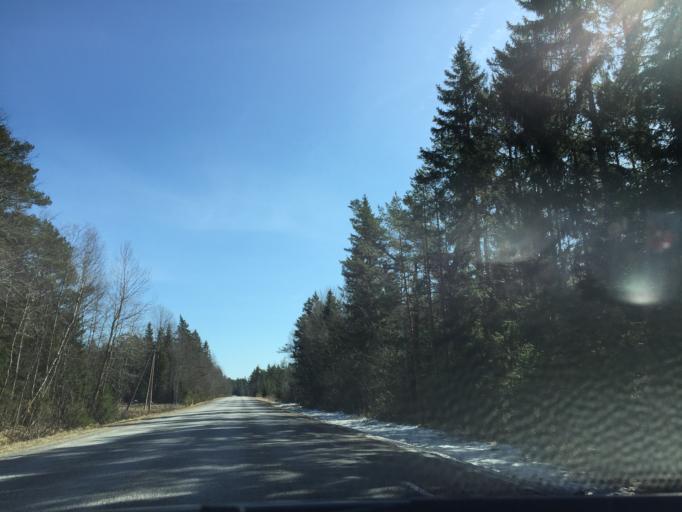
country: EE
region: Laeaene
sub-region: Lihula vald
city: Lihula
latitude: 58.5405
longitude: 23.9273
